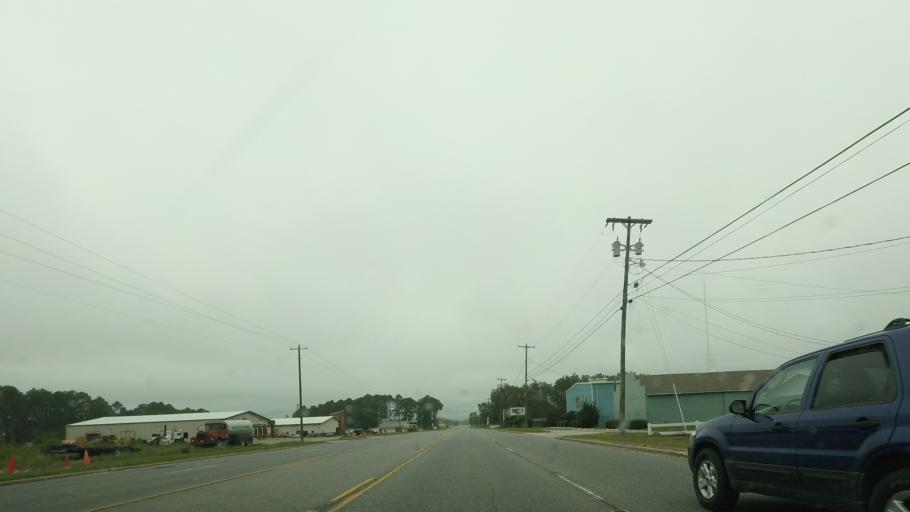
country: US
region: Georgia
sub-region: Irwin County
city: Ocilla
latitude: 31.6194
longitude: -83.2498
